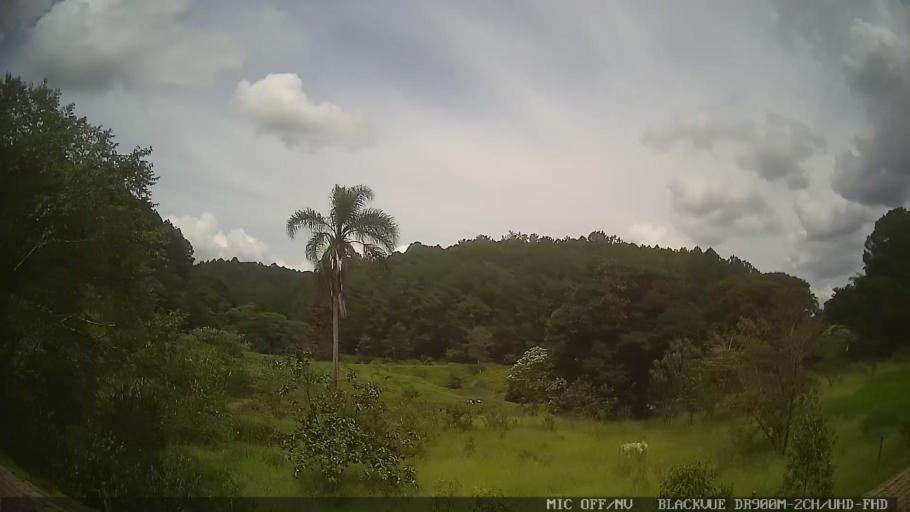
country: BR
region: Sao Paulo
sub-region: Atibaia
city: Atibaia
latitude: -23.0826
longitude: -46.5517
